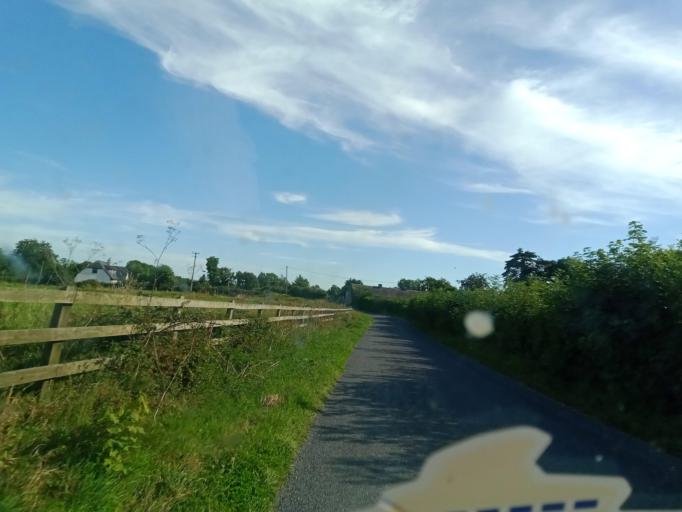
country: IE
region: Leinster
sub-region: Kilkenny
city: Ballyragget
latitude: 52.7760
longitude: -7.3891
